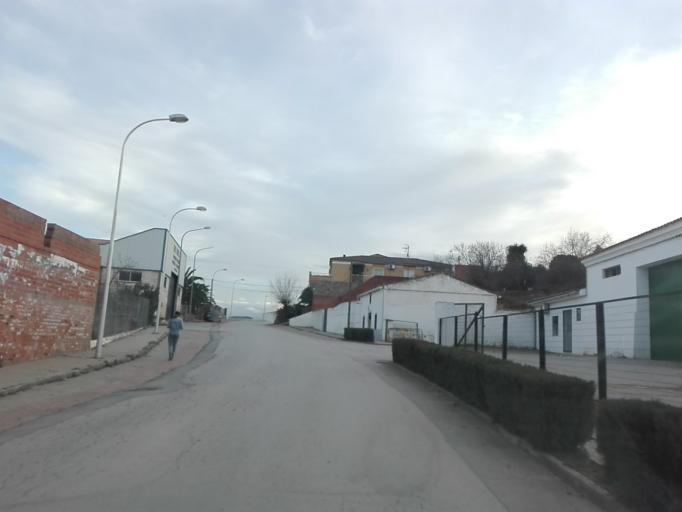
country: ES
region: Extremadura
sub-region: Provincia de Badajoz
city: Usagre
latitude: 38.3542
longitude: -6.1710
